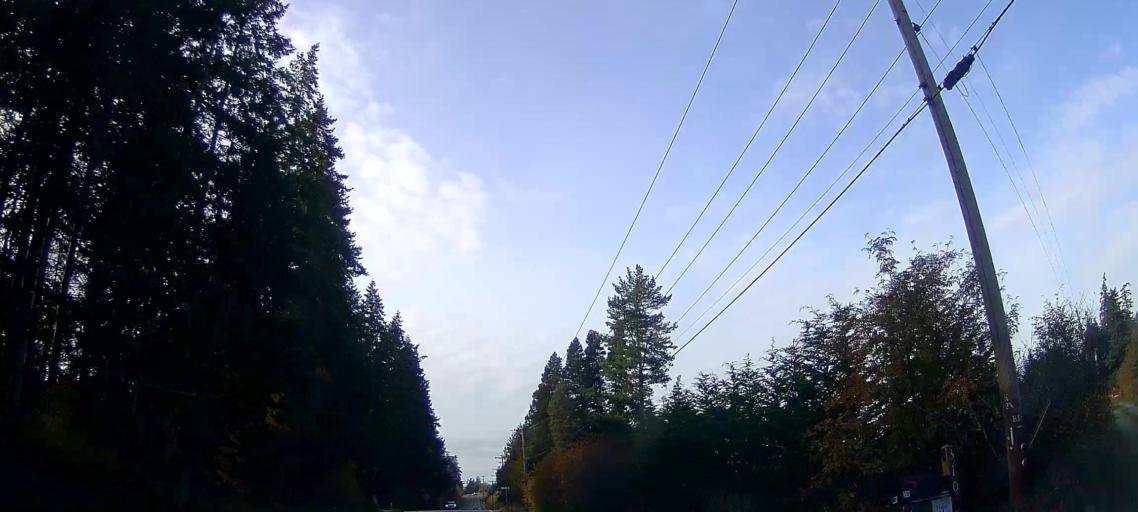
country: US
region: Washington
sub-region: Snohomish County
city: Stanwood
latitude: 48.2498
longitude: -122.4634
